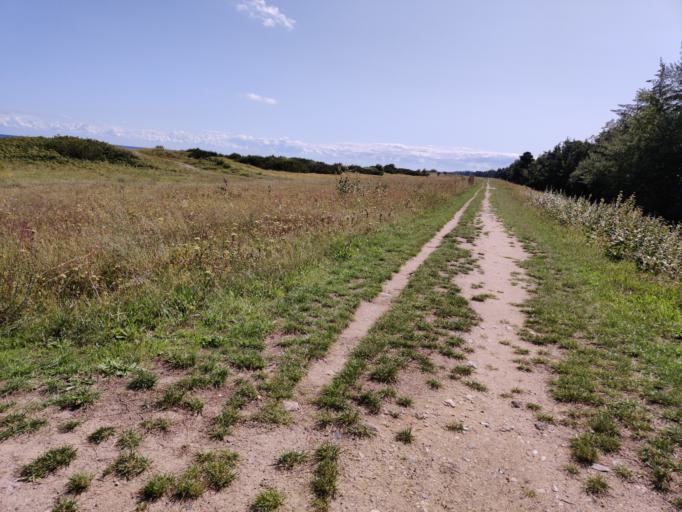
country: DK
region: Zealand
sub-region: Guldborgsund Kommune
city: Nykobing Falster
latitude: 54.6654
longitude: 11.9602
